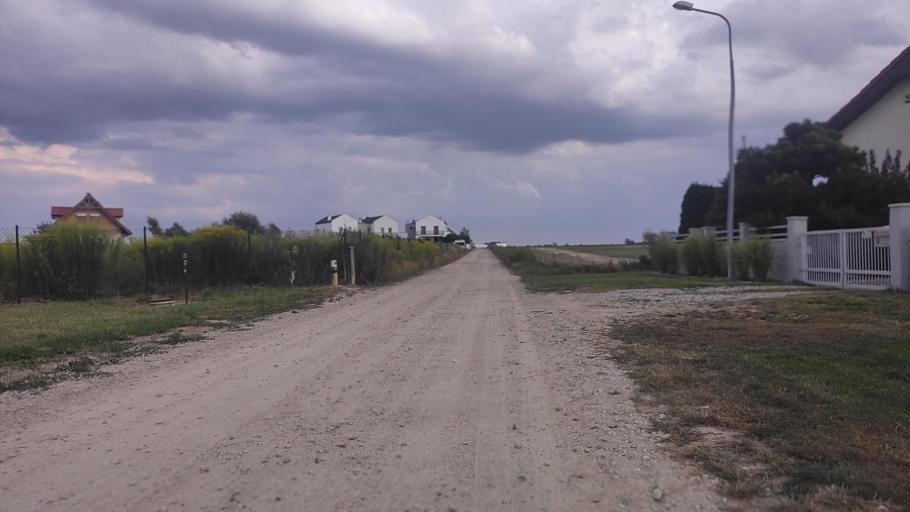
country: PL
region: Greater Poland Voivodeship
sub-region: Powiat poznanski
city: Swarzedz
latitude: 52.4240
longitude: 17.1132
